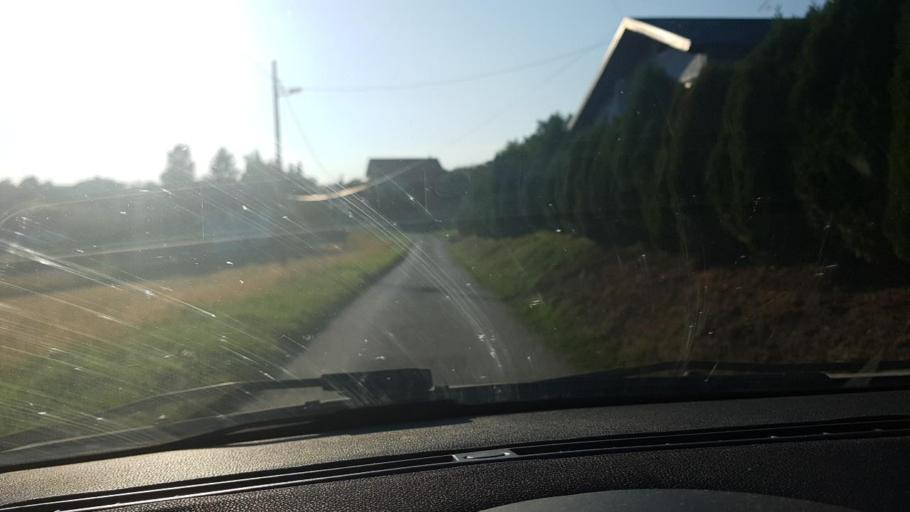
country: HR
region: Krapinsko-Zagorska
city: Radoboj
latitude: 46.1635
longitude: 15.9384
